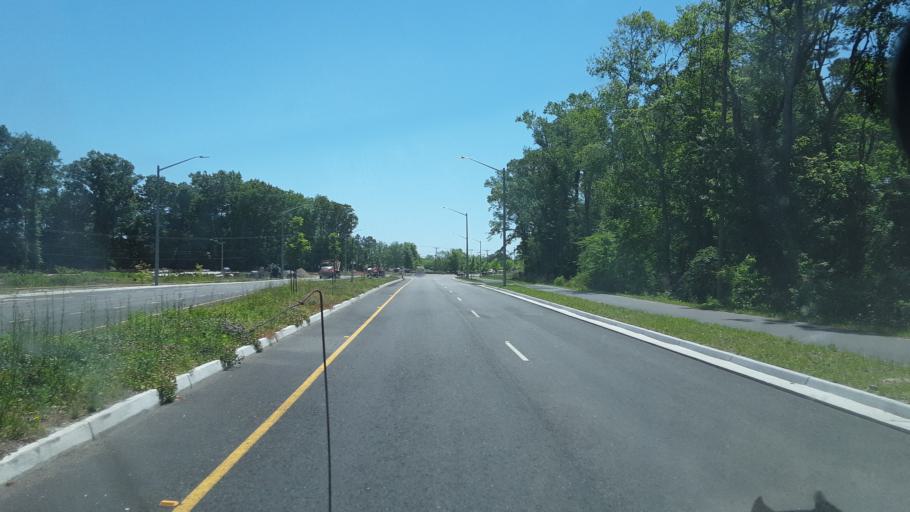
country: US
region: Virginia
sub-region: City of Virginia Beach
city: Virginia Beach
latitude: 36.7586
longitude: -76.0157
